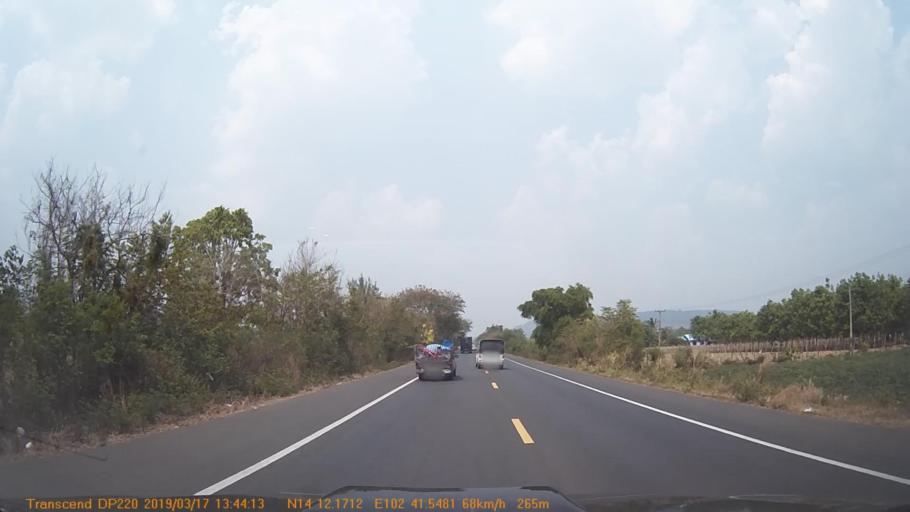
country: TH
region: Buriram
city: Non Din Daeng
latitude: 14.2033
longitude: 102.6926
